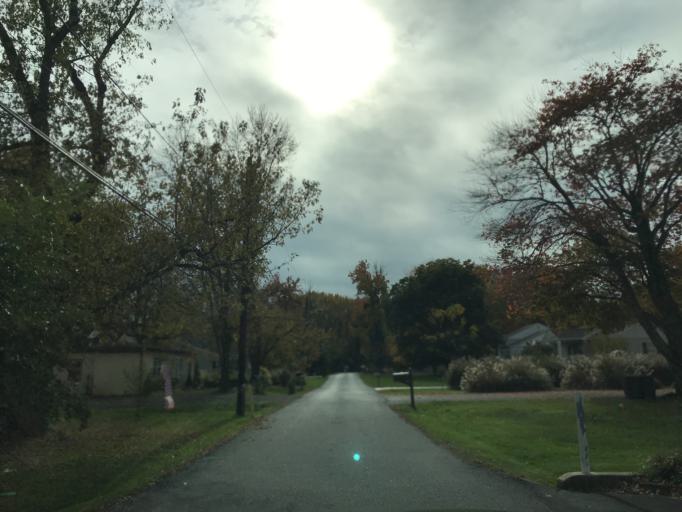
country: US
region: Maryland
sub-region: Baltimore County
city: Bowleys Quarters
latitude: 39.3123
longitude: -76.3951
